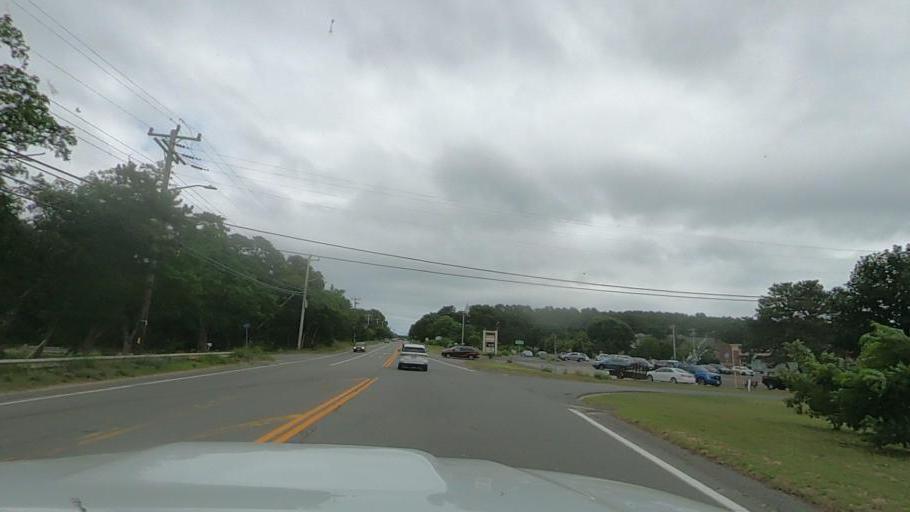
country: US
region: Massachusetts
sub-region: Barnstable County
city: Wellfleet
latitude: 41.9302
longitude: -70.0173
